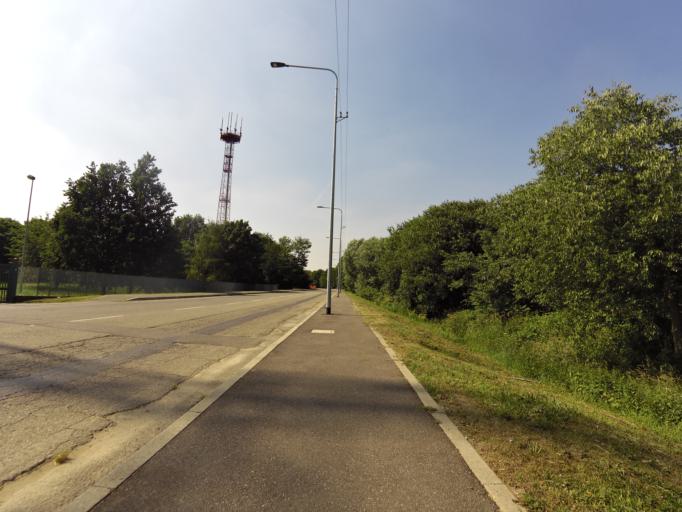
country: IT
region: Lombardy
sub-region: Citta metropolitana di Milano
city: Linate
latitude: 45.4560
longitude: 9.2589
